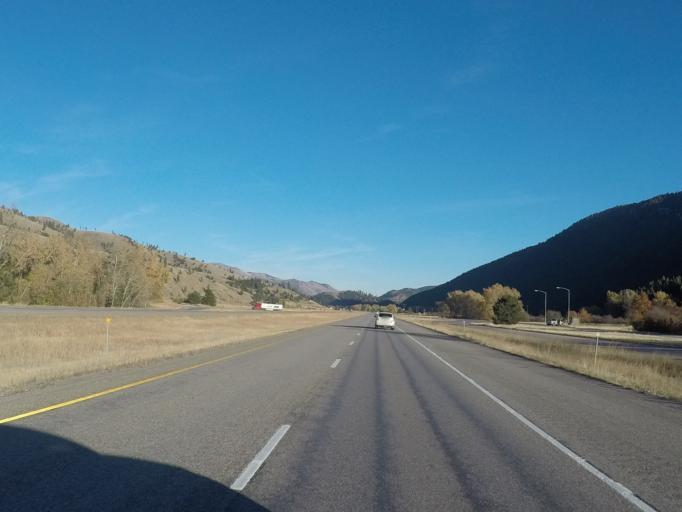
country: US
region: Montana
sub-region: Missoula County
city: Clinton
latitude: 46.7270
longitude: -113.6427
